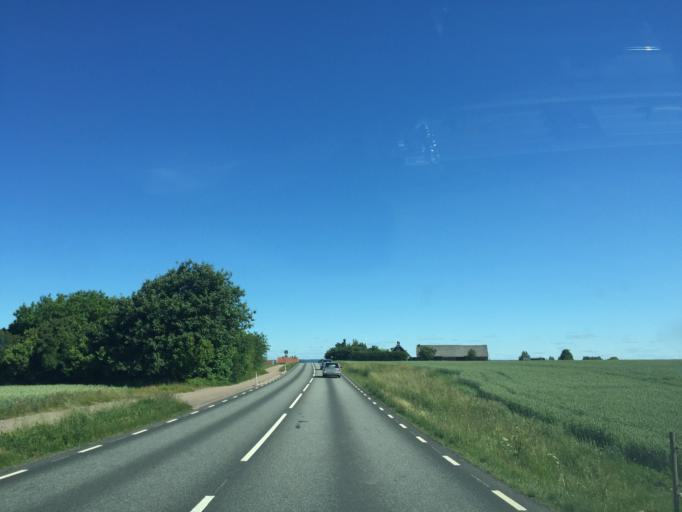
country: SE
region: Skane
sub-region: Angelholms Kommun
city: AEngelholm
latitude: 56.2070
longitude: 12.8553
